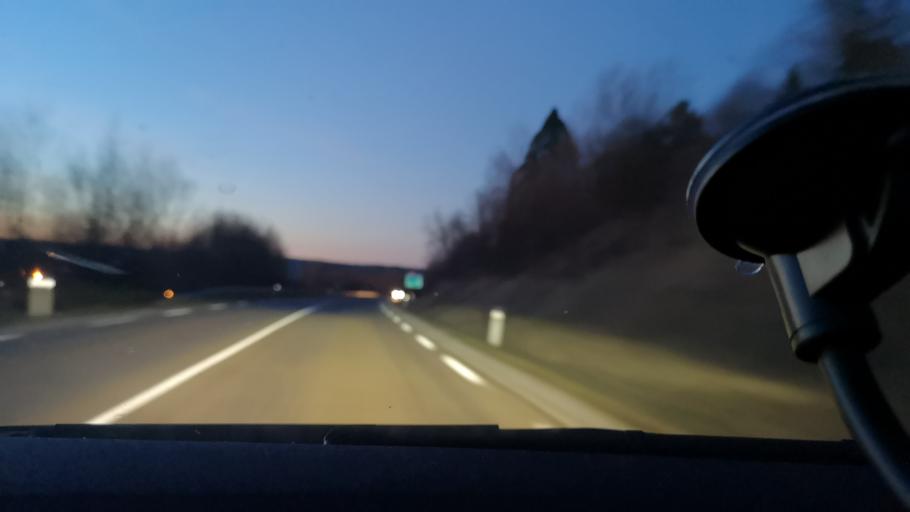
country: FR
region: Franche-Comte
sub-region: Departement du Jura
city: Champagnole
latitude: 46.7550
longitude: 5.9128
